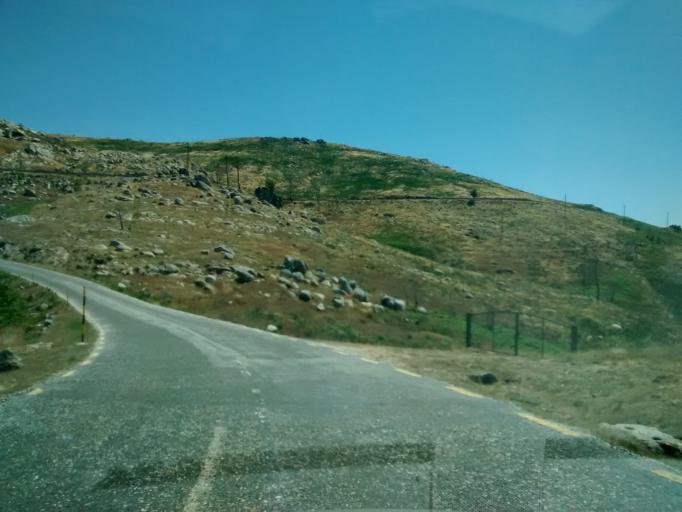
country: PT
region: Guarda
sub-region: Manteigas
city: Manteigas
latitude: 40.4226
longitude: -7.6193
